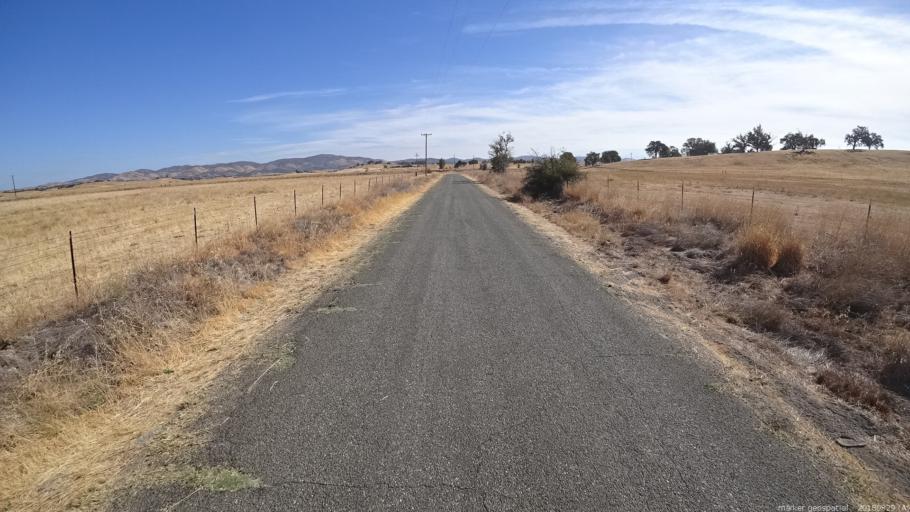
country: US
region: California
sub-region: Monterey County
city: King City
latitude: 35.9388
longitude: -121.1219
